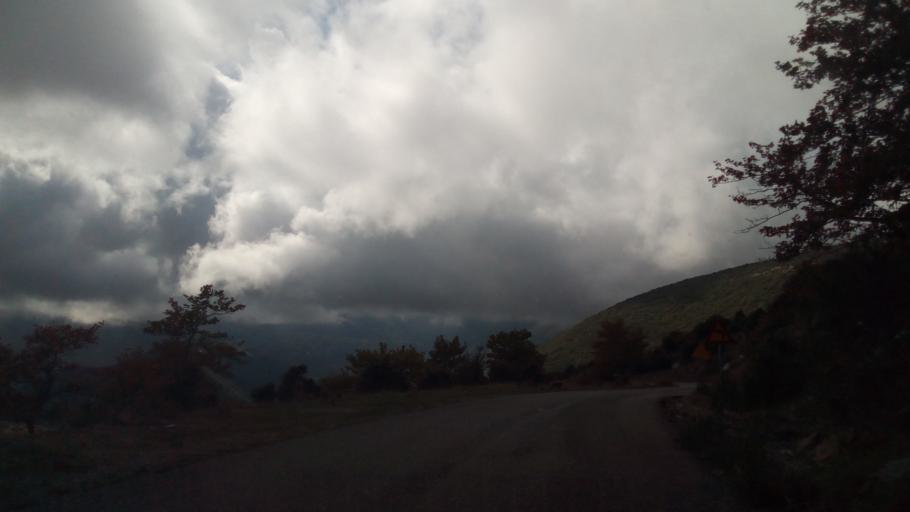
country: GR
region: West Greece
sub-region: Nomos Aitolias kai Akarnanias
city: Thermo
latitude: 38.5425
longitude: 21.8123
